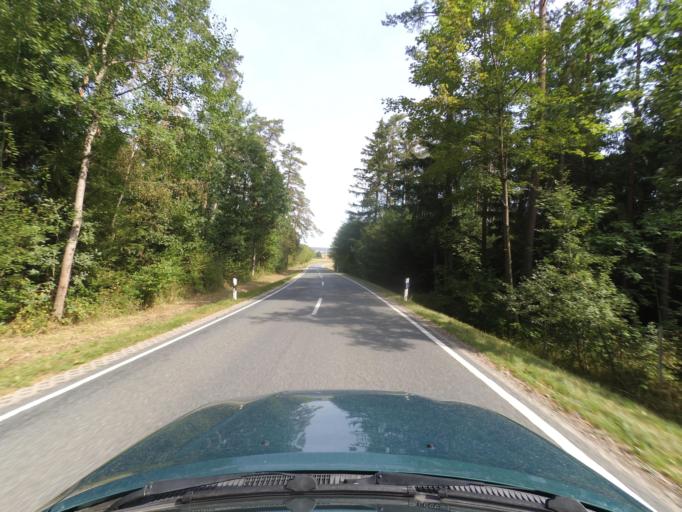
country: DE
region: Bavaria
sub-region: Regierungsbezirk Mittelfranken
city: Wieseth
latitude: 49.2093
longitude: 10.4555
